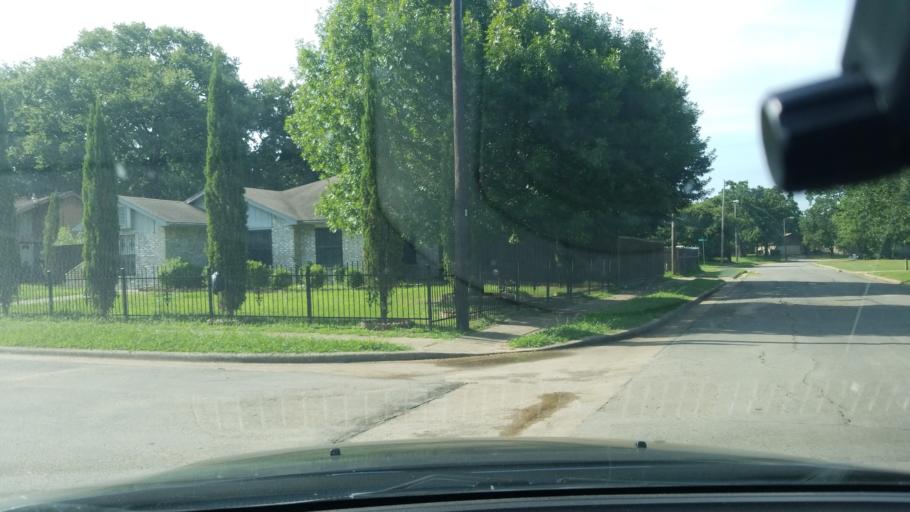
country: US
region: Texas
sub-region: Dallas County
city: Balch Springs
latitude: 32.7293
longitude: -96.6416
